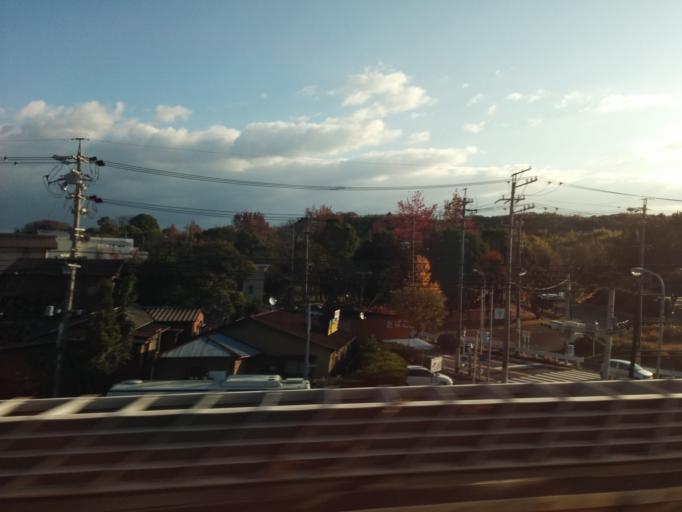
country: JP
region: Aichi
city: Obu
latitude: 35.0624
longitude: 136.9445
